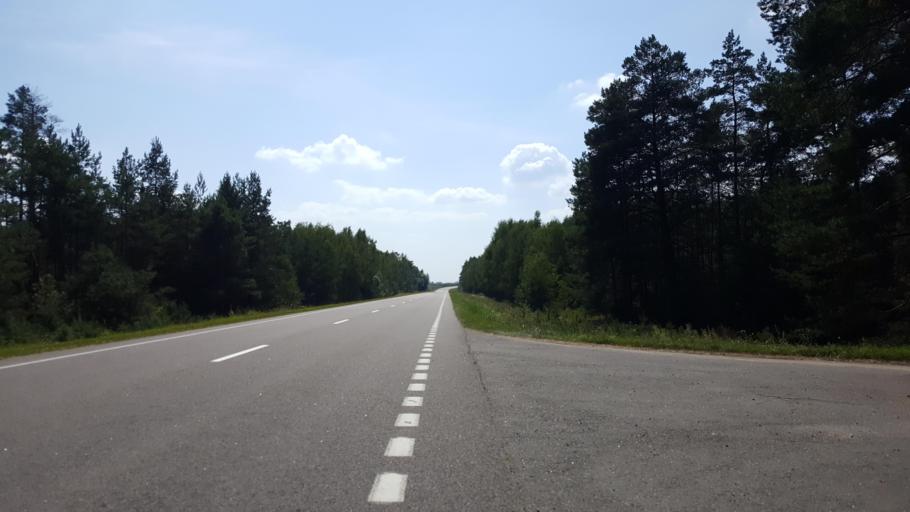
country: PL
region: Podlasie
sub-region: Powiat hajnowski
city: Czeremcha
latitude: 52.5204
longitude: 23.5348
